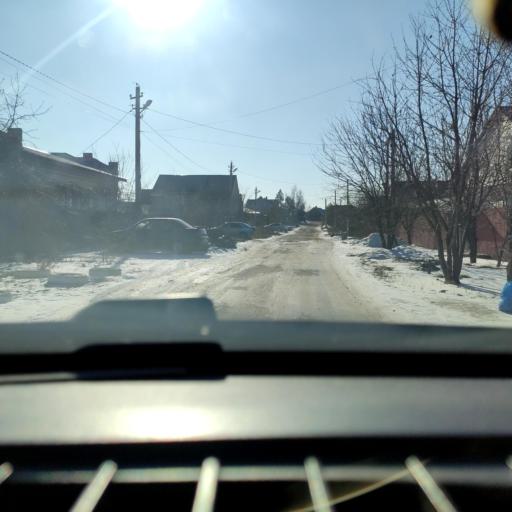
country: RU
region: Voronezj
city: Somovo
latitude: 51.6837
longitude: 39.3142
